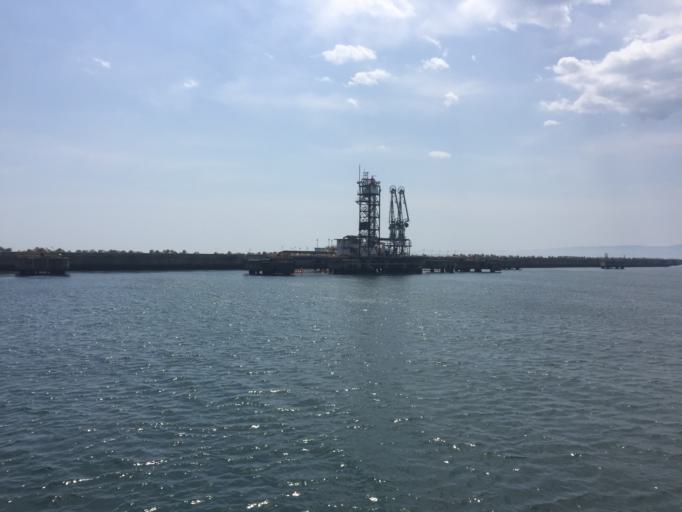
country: JP
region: Fukushima
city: Iwaki
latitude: 36.9220
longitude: 140.8815
